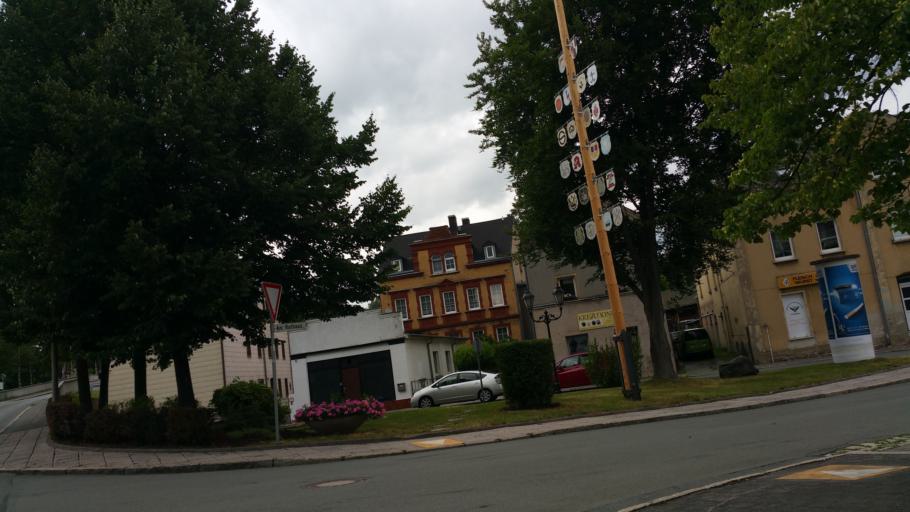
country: DE
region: Bavaria
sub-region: Upper Franconia
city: Oberkotzau
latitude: 50.2642
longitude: 11.9335
